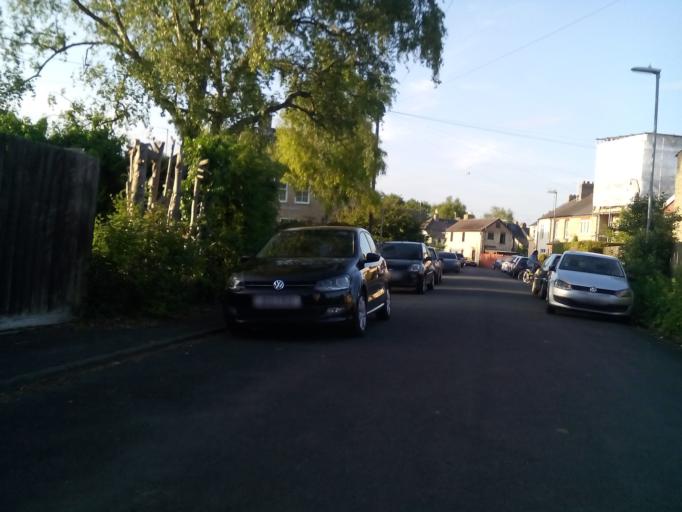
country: GB
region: England
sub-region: Cambridgeshire
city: Cambridge
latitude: 52.1952
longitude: 0.1536
